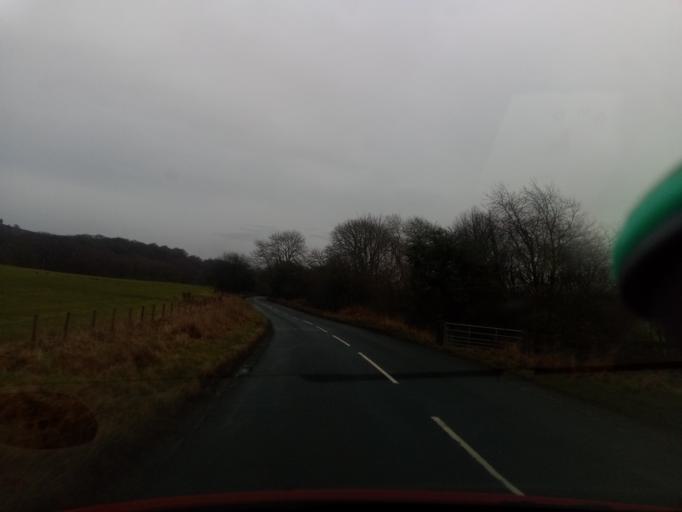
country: GB
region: England
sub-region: Northumberland
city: Rochester
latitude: 55.1563
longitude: -2.2964
